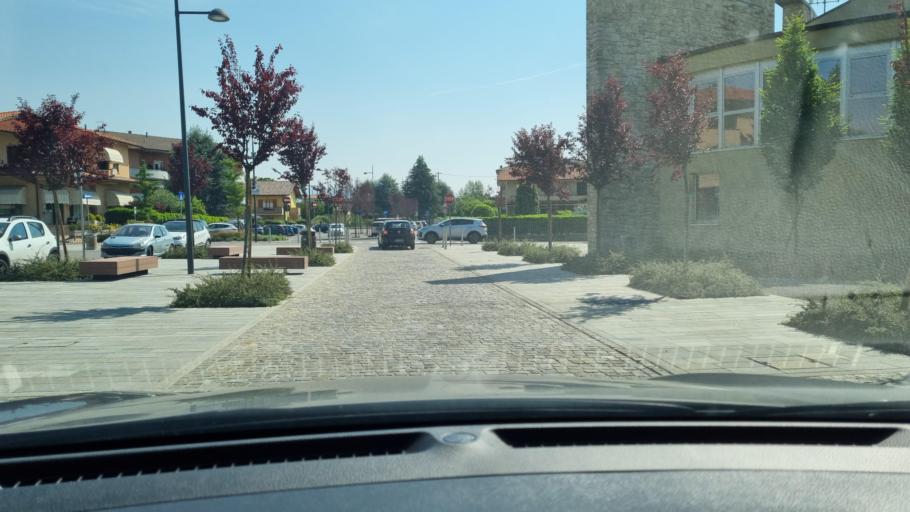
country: IT
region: Lombardy
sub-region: Provincia di Bergamo
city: Ambivere
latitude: 45.7187
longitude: 9.5490
